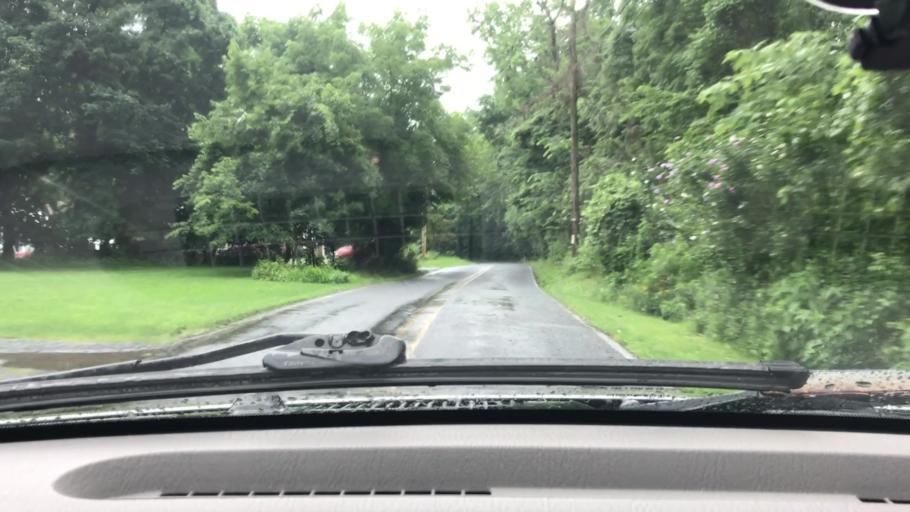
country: US
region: Pennsylvania
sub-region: Lancaster County
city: Elizabethtown
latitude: 40.2120
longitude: -76.6209
